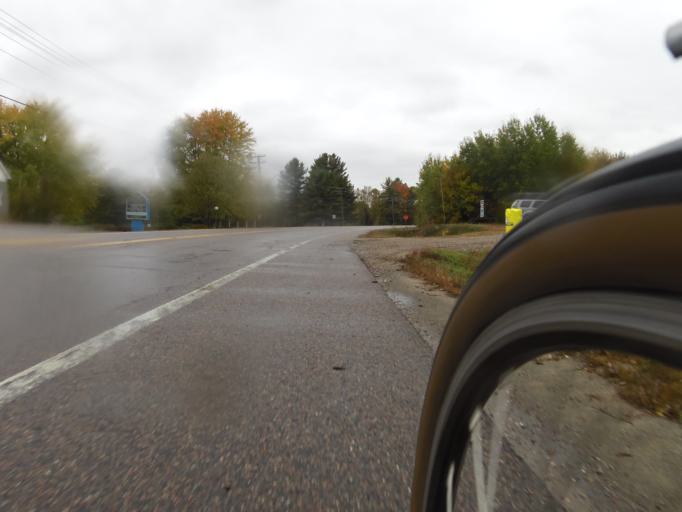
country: CA
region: Quebec
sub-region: Outaouais
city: Fort-Coulonge
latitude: 45.8550
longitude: -76.7383
